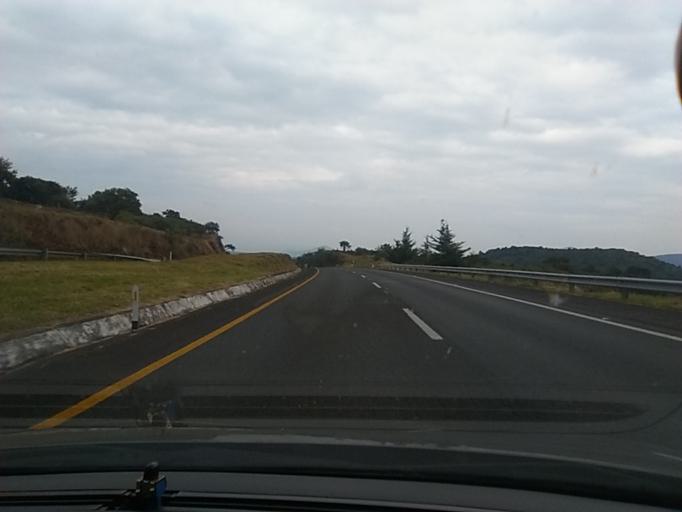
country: MX
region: Michoacan
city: Panindicuaro de la Reforma
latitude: 19.9962
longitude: -101.8626
